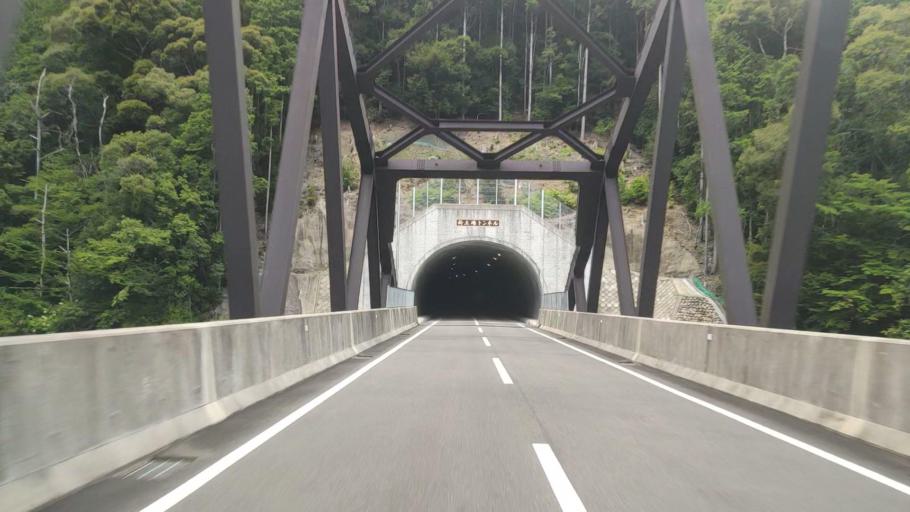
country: JP
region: Mie
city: Owase
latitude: 34.0031
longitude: 136.0095
